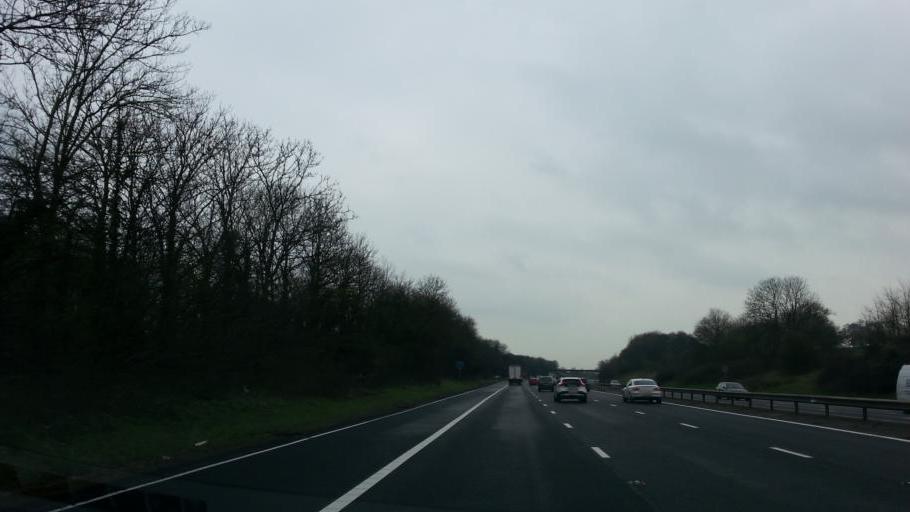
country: GB
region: England
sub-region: Gloucestershire
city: Dursley
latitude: 51.6987
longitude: -2.3922
